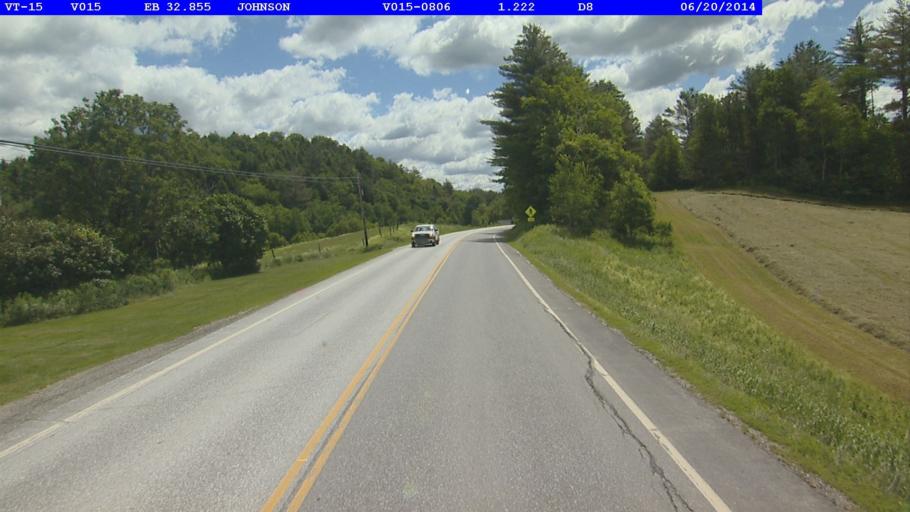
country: US
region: Vermont
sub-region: Lamoille County
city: Johnson
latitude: 44.6457
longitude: -72.7308
